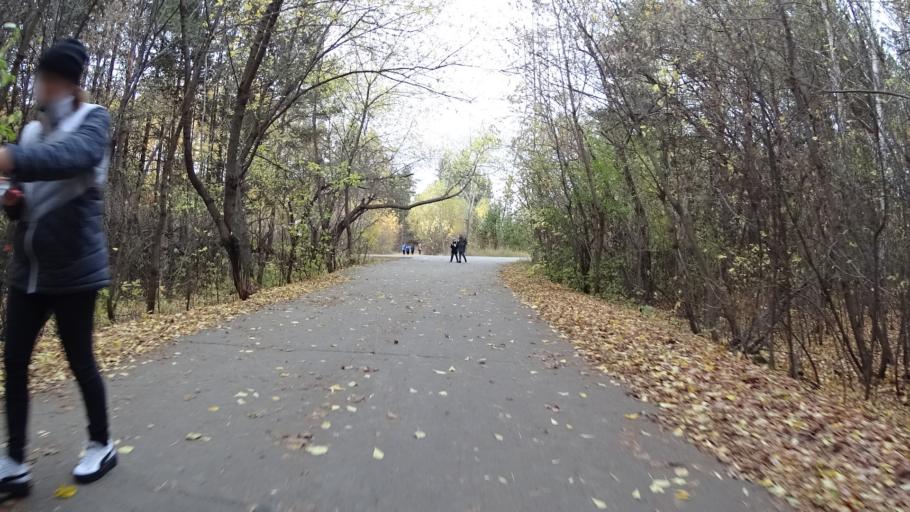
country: RU
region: Chelyabinsk
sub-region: Gorod Chelyabinsk
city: Chelyabinsk
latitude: 55.1574
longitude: 61.3592
